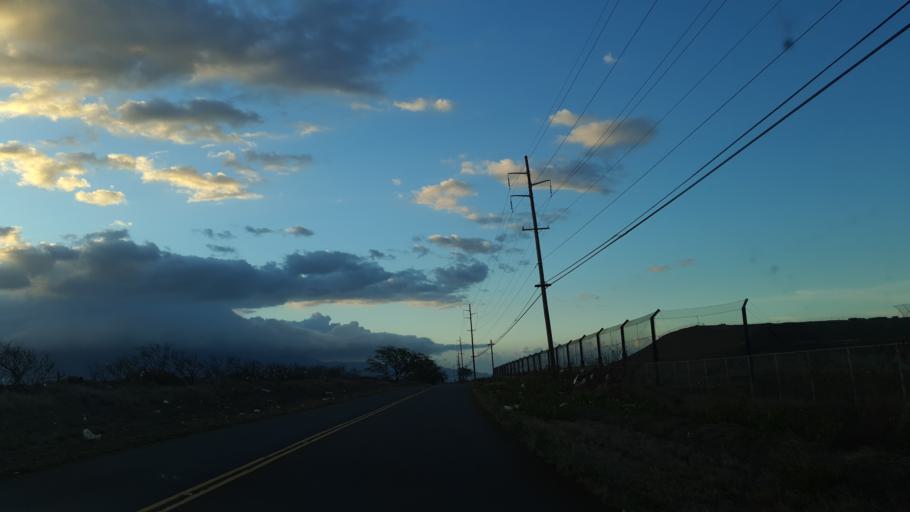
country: US
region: Hawaii
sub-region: Maui County
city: Kahului
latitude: 20.8545
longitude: -156.4211
